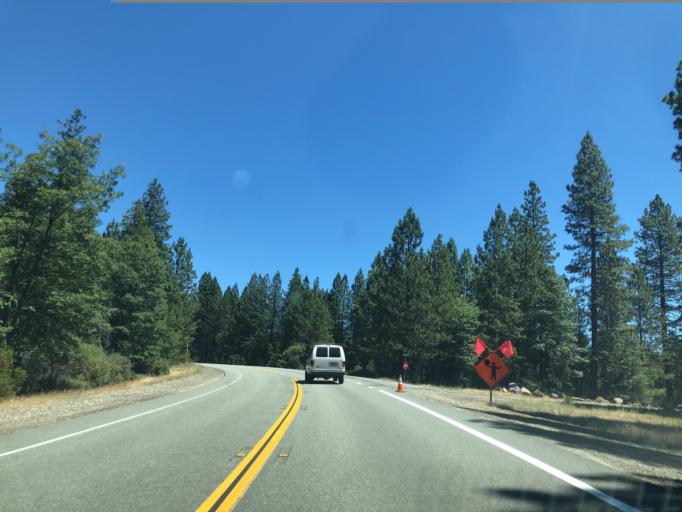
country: US
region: California
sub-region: Shasta County
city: Shingletown
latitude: 40.4900
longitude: -121.8967
